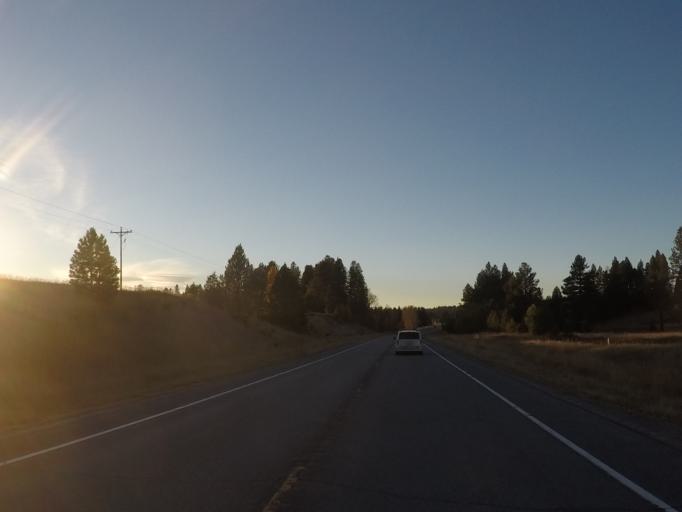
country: US
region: Montana
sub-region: Lewis and Clark County
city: Lincoln
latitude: 46.9978
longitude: -113.0311
